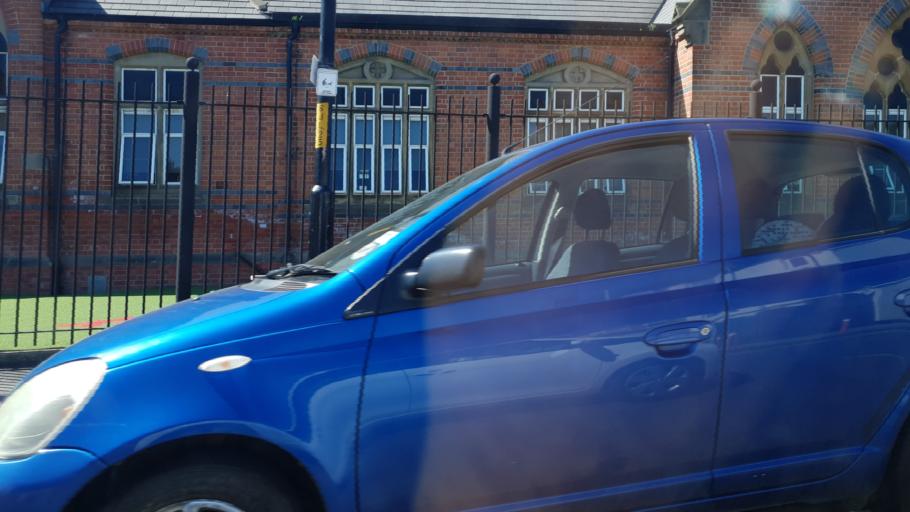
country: GB
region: England
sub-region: Middlesbrough
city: Middlesbrough
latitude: 54.5583
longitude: -1.2482
